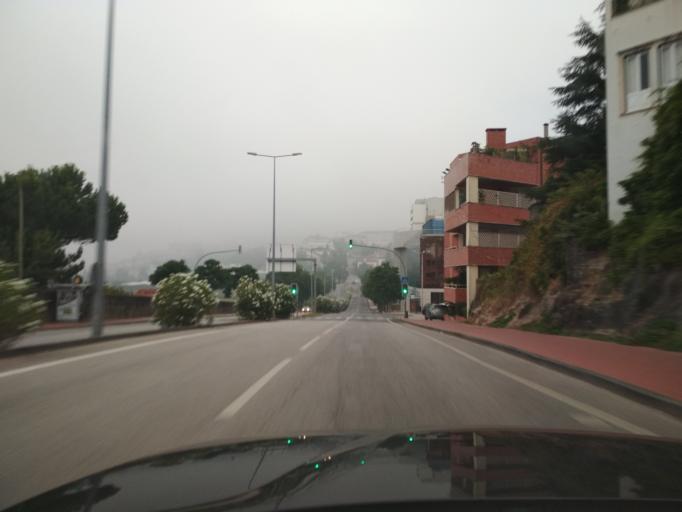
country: PT
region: Coimbra
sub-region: Coimbra
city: Coimbra
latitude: 40.1942
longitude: -8.4208
